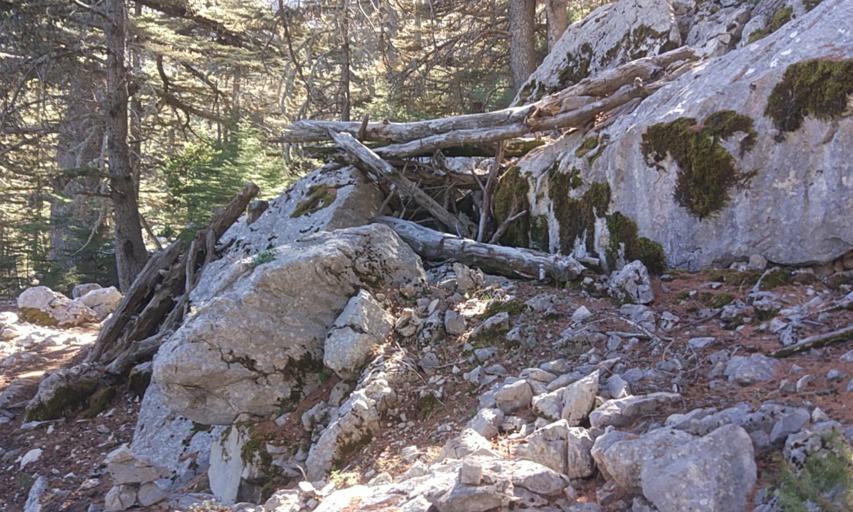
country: TR
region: Antalya
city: Altinyaka
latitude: 36.5561
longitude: 30.4158
